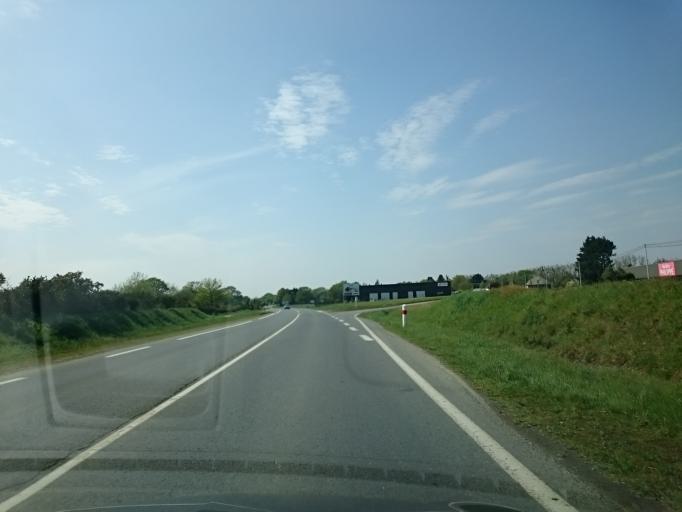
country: FR
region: Brittany
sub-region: Departement d'Ille-et-Vilaine
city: Chantepie
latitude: 48.0789
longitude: -1.5972
